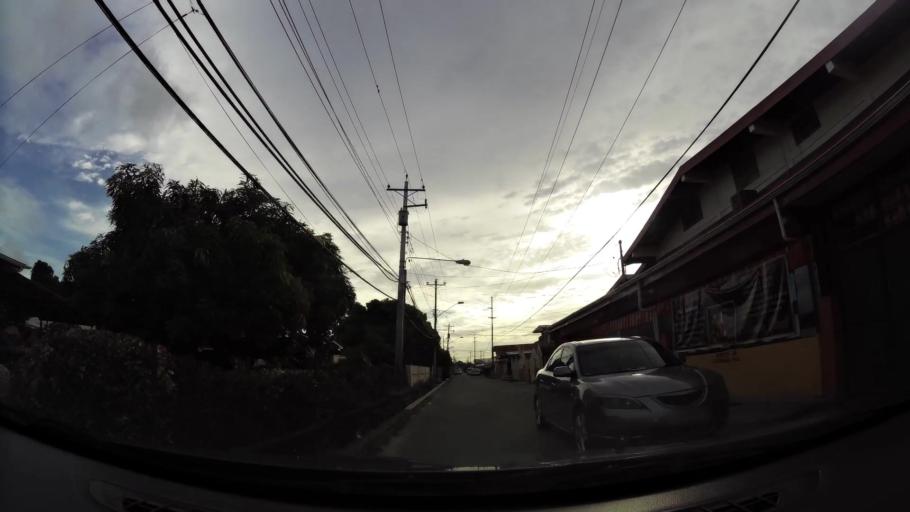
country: TT
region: Tunapuna/Piarco
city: Tunapuna
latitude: 10.6390
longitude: -61.4079
